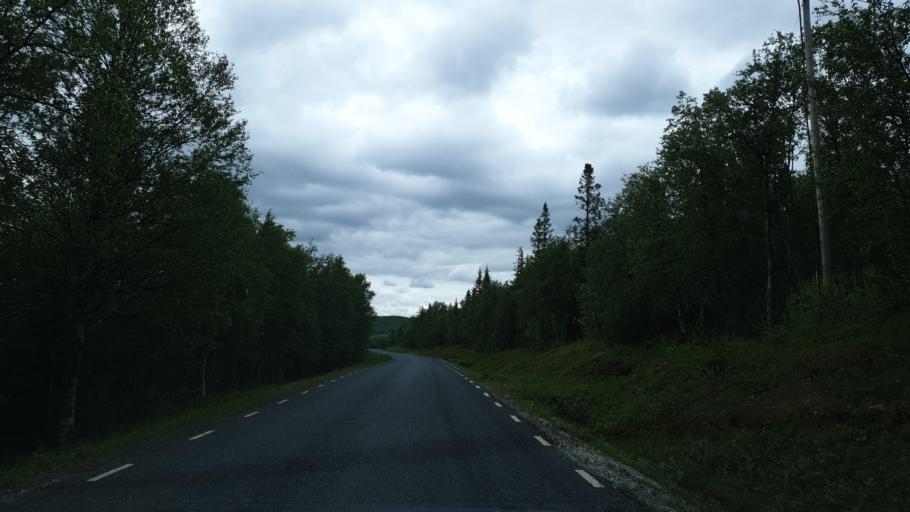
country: SE
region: Vaesterbotten
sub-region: Vilhelmina Kommun
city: Sjoberg
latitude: 65.2839
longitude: 15.2971
